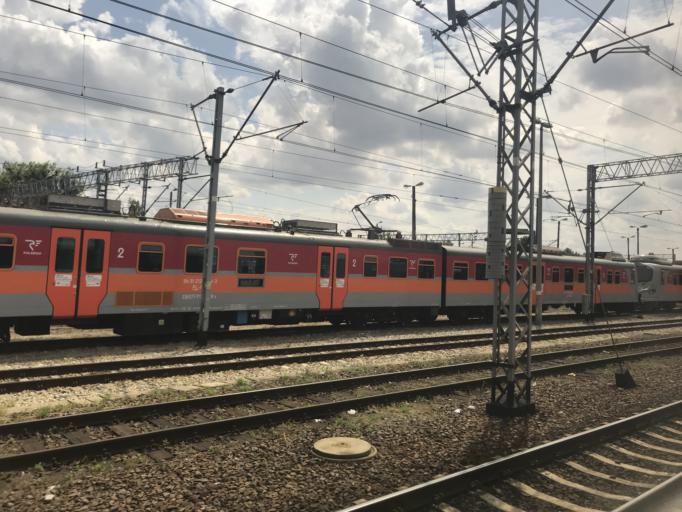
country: PL
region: Greater Poland Voivodeship
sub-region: Poznan
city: Poznan
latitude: 52.3964
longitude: 16.9096
